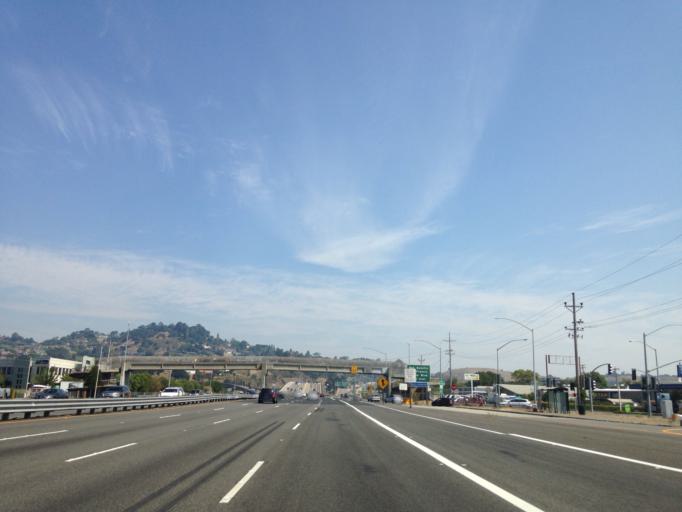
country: US
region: California
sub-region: Marin County
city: Corte Madera
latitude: 37.9381
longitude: -122.5165
